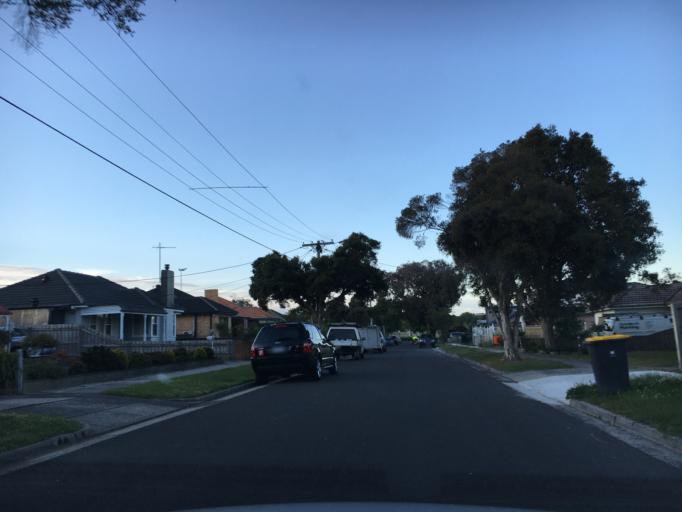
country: AU
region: Victoria
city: Clayton
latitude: -37.9114
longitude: 145.1164
